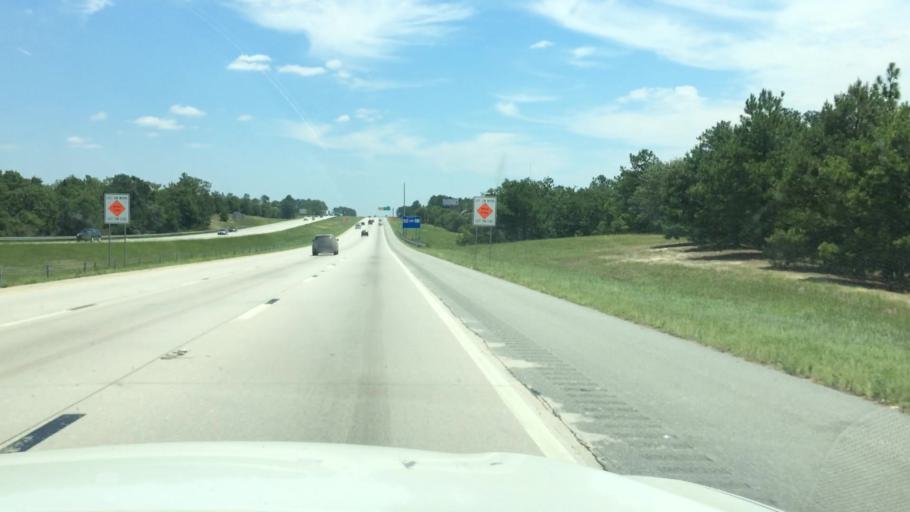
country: US
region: South Carolina
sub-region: Kershaw County
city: Elgin
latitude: 34.1004
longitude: -80.8410
